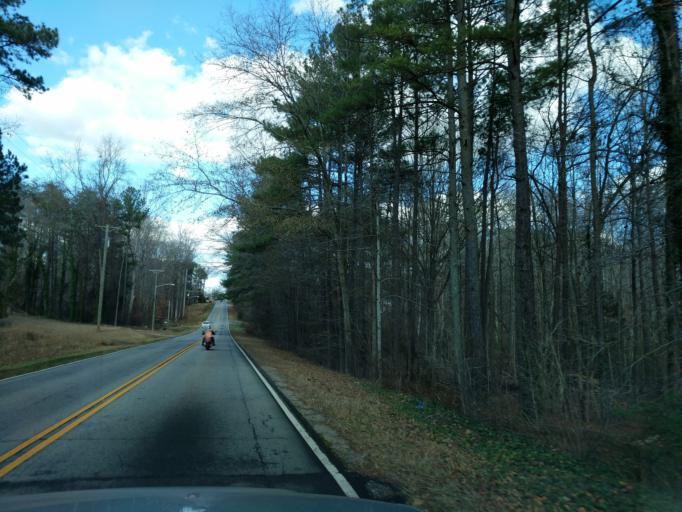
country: US
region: South Carolina
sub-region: Laurens County
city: Laurens
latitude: 34.4799
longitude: -82.0241
